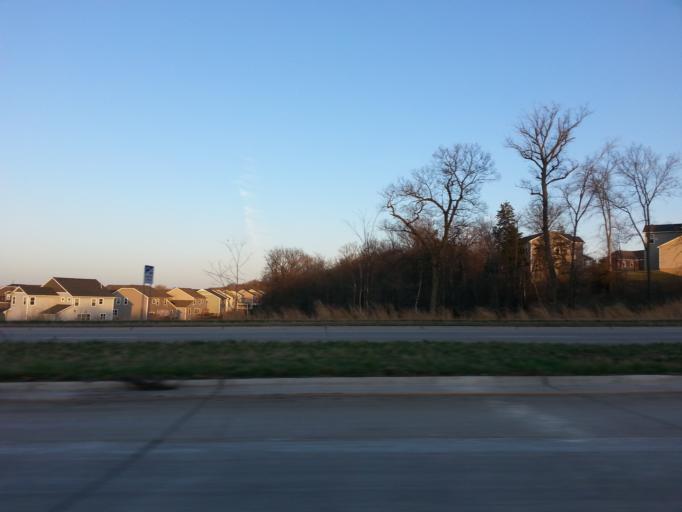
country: US
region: Minnesota
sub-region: Scott County
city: Prior Lake
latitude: 44.7694
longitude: -93.4351
